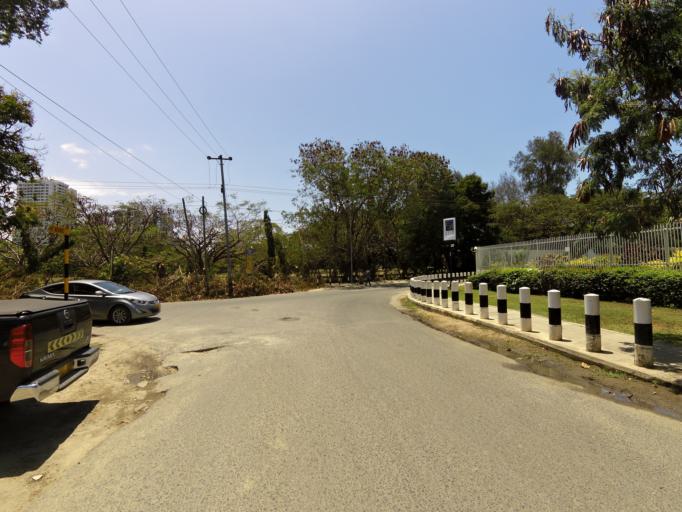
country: TZ
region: Dar es Salaam
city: Dar es Salaam
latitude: -6.8116
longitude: 39.2904
